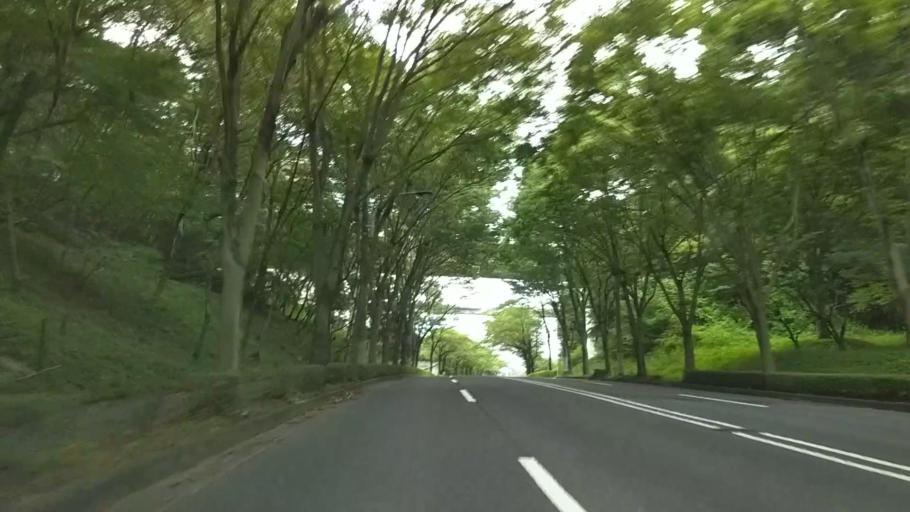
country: JP
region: Tokyo
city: Hachioji
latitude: 35.6164
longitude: 139.2968
